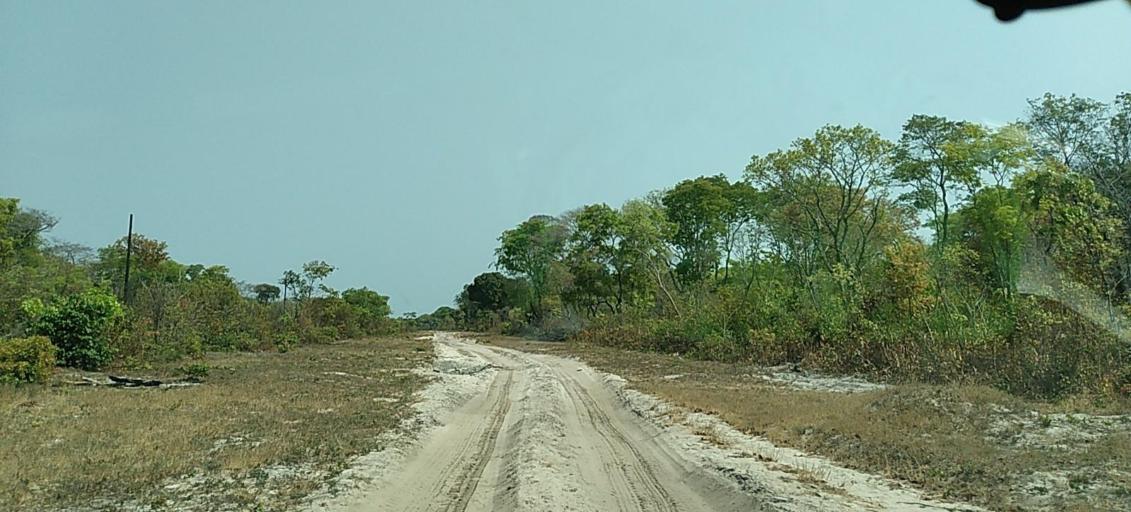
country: ZM
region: North-Western
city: Kabompo
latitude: -13.2417
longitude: 24.0165
